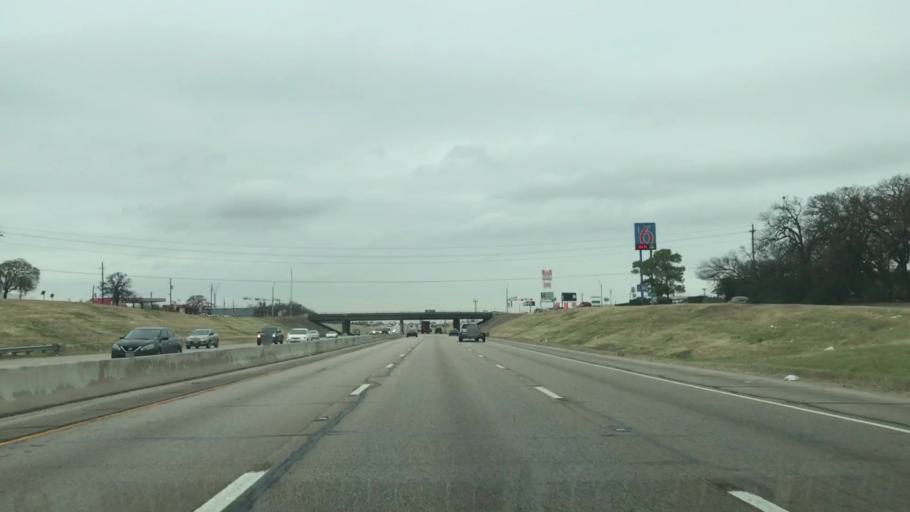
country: US
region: Texas
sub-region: Dallas County
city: Irving
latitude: 32.8071
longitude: -96.9216
